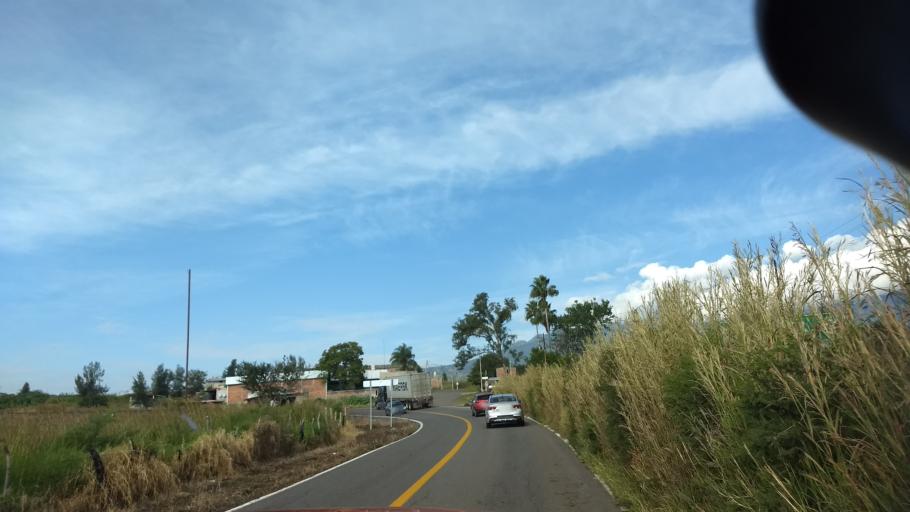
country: MX
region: Jalisco
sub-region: Tonila
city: San Marcos
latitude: 19.4381
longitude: -103.5082
